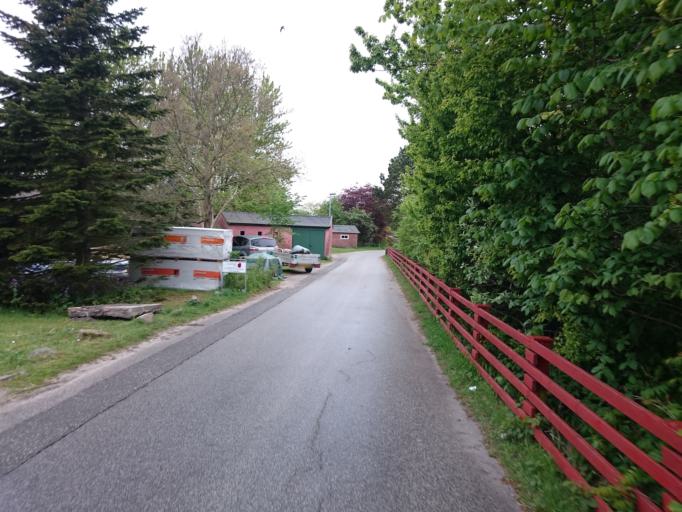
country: DK
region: South Denmark
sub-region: Fano Kommune
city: Nordby
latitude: 55.4479
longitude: 8.4013
